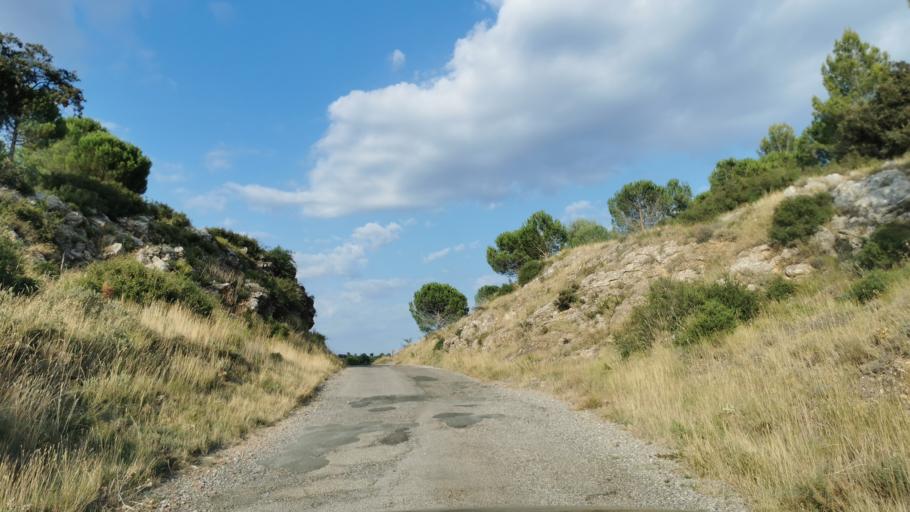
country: FR
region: Languedoc-Roussillon
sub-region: Departement de l'Aude
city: Bizanet
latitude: 43.1702
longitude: 2.8863
